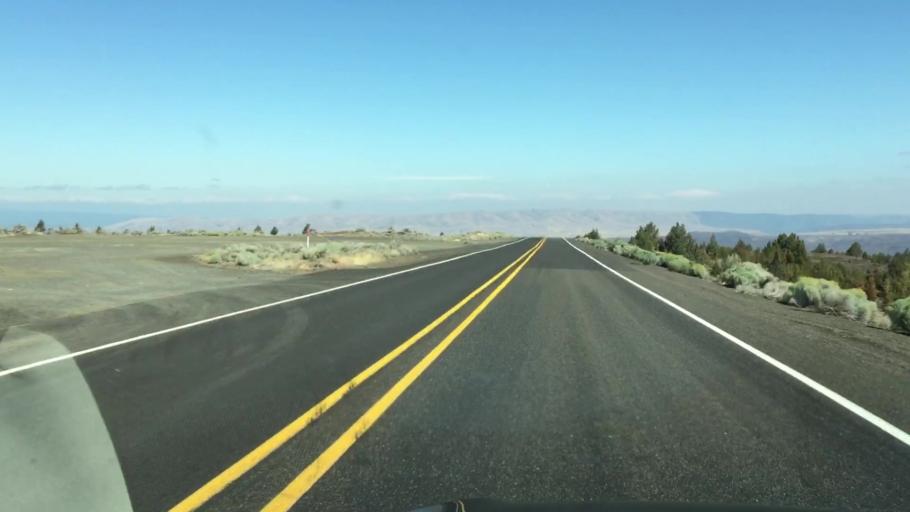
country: US
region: Oregon
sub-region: Jefferson County
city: Warm Springs
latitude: 45.0853
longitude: -121.0265
